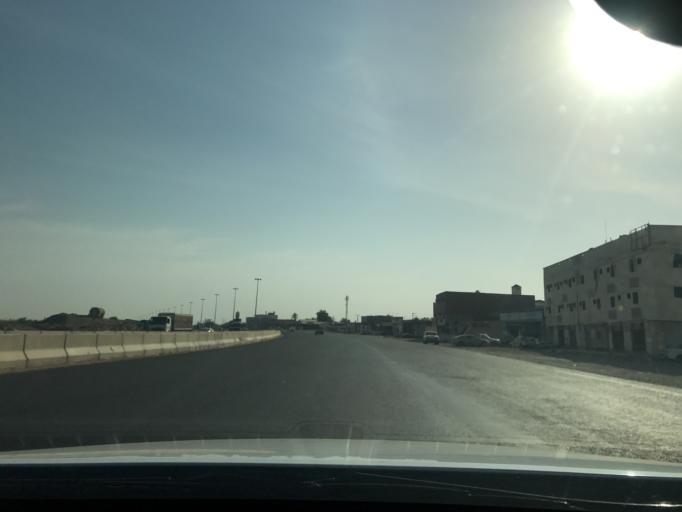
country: SA
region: Makkah
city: Al Jumum
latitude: 21.4392
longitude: 39.5262
